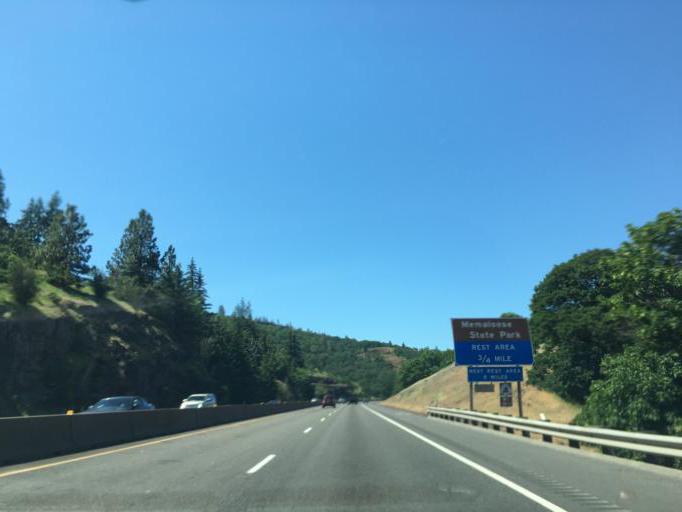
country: US
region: Oregon
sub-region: Wasco County
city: Chenoweth
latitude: 45.6939
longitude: -121.3219
